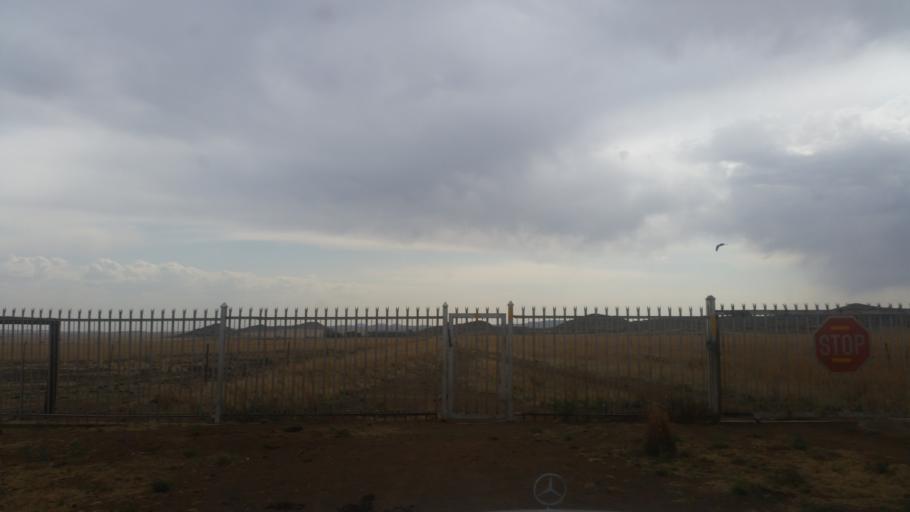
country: ZA
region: Orange Free State
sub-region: Xhariep District Municipality
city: Trompsburg
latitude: -30.5070
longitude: 25.9201
